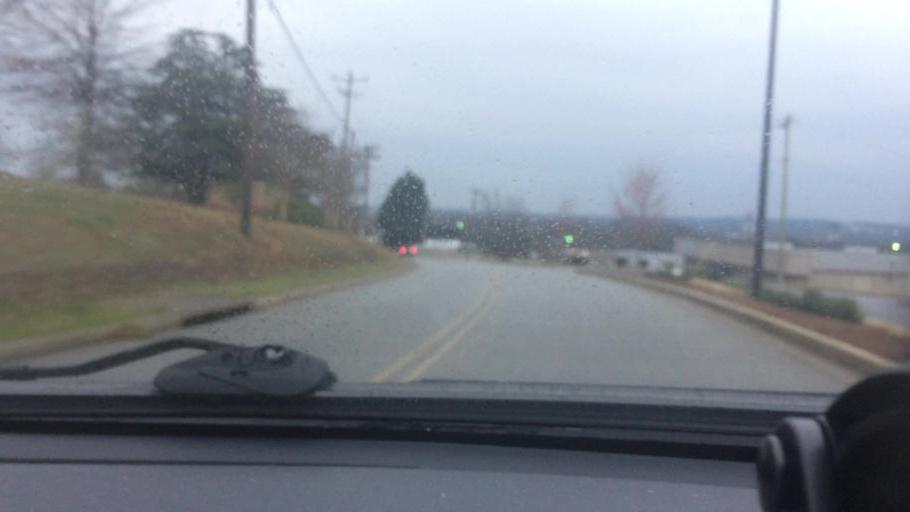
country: US
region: South Carolina
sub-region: Greenville County
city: Wade Hampton
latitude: 34.8968
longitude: -82.3741
